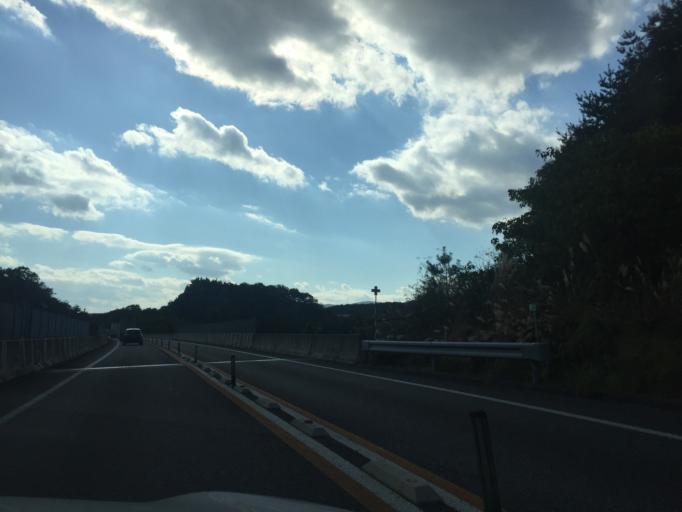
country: JP
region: Fukushima
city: Iwaki
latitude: 37.0903
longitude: 140.8436
